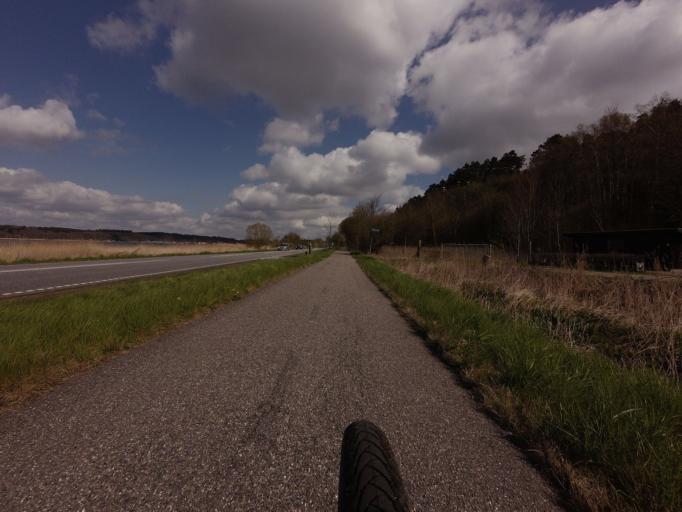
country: DK
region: North Denmark
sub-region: Mariagerfjord Kommune
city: Hadsund
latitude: 56.6980
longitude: 10.1132
